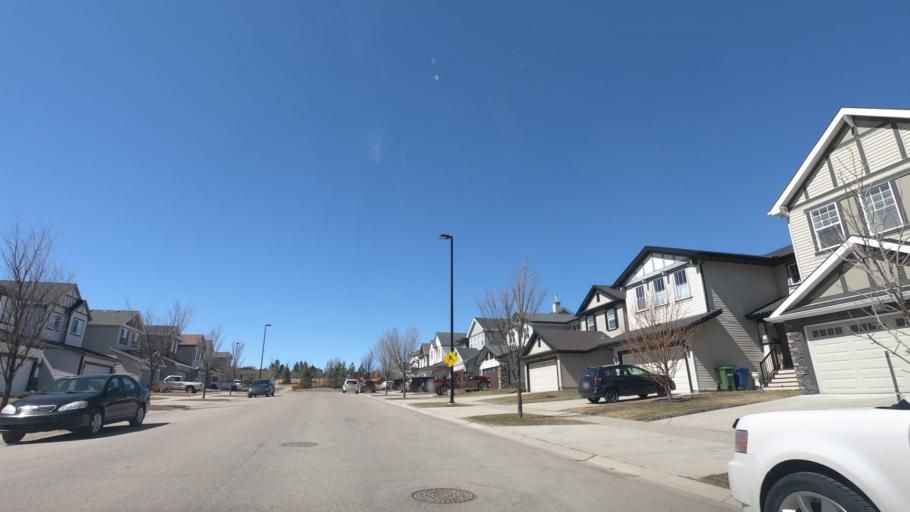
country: CA
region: Alberta
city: Airdrie
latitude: 51.3031
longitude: -114.0454
